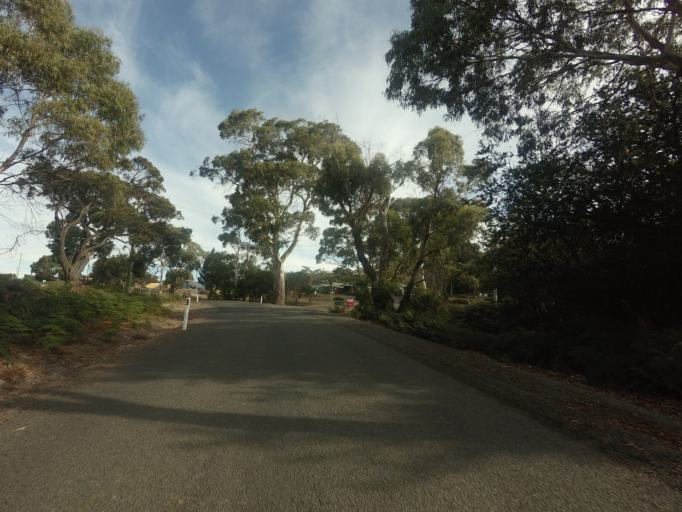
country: AU
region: Tasmania
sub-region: Sorell
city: Sorell
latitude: -42.9654
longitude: 147.8312
